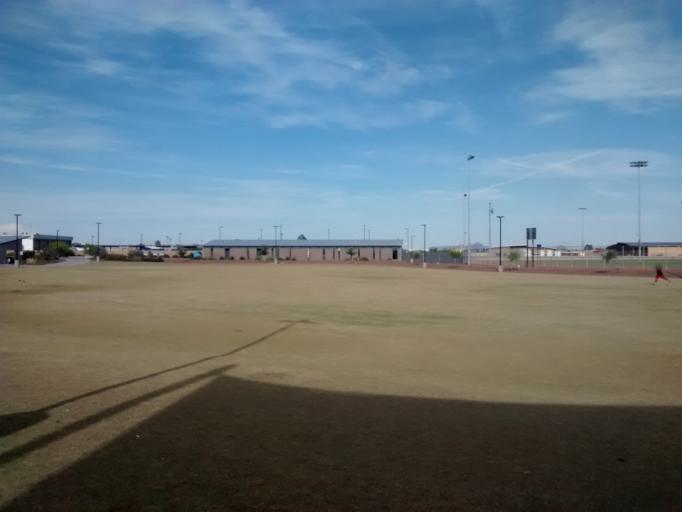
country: US
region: Arizona
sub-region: Maricopa County
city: Peoria
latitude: 33.5630
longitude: -112.2353
